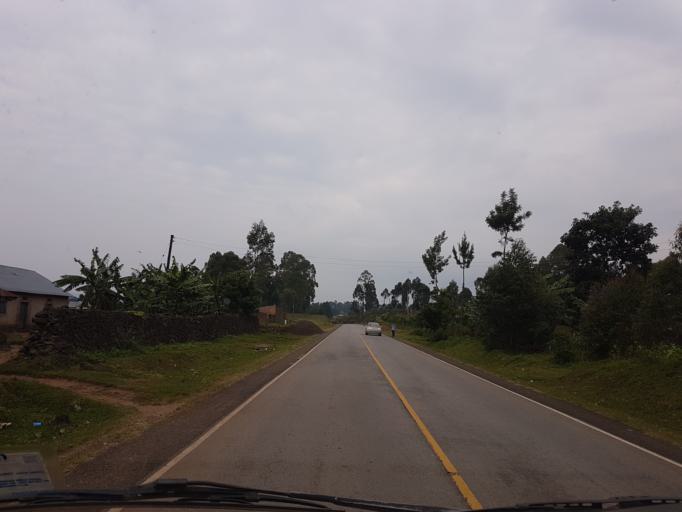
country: UG
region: Western Region
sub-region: Kisoro District
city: Kisoro
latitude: -1.3171
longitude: 29.7263
